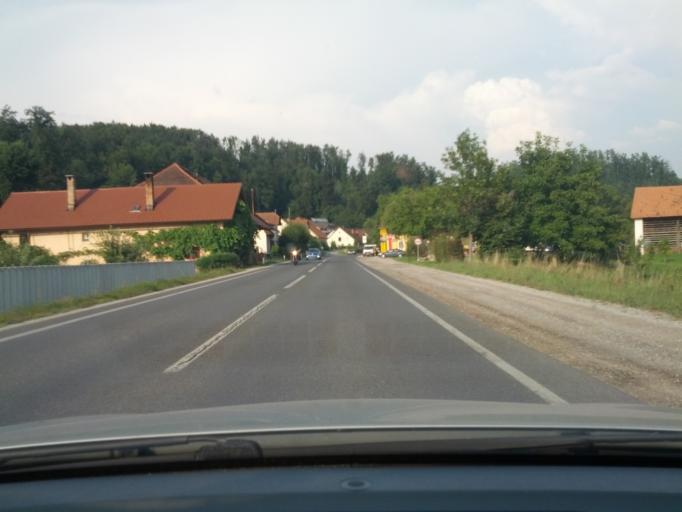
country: SI
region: Log-Dragomer
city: Log pri Brezovici
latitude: 46.0073
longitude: 14.3572
